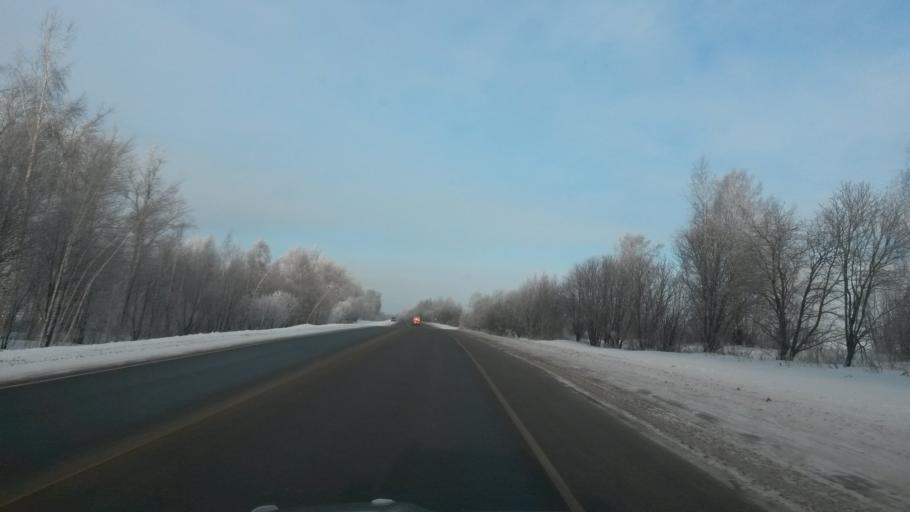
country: RU
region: Vladimir
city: Bogolyubovo
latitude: 56.2002
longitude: 40.4458
